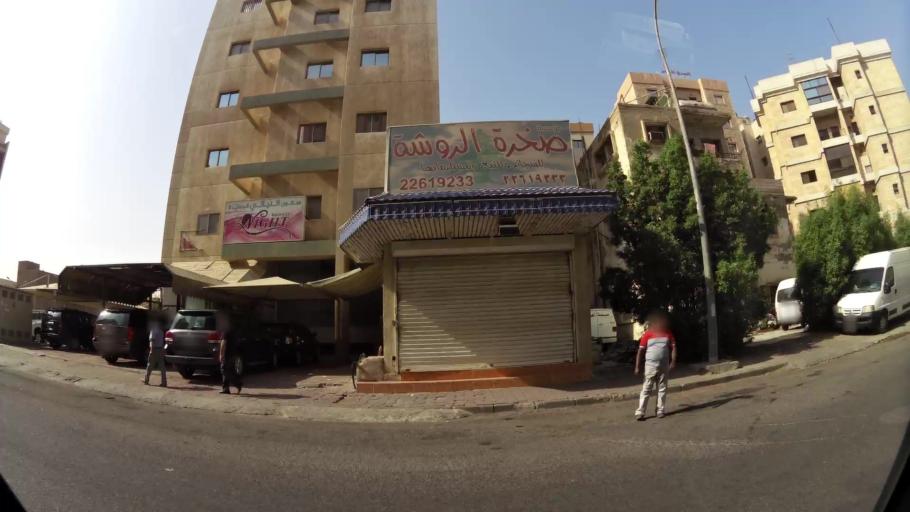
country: KW
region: Muhafazat Hawalli
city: Hawalli
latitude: 29.3369
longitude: 48.0120
